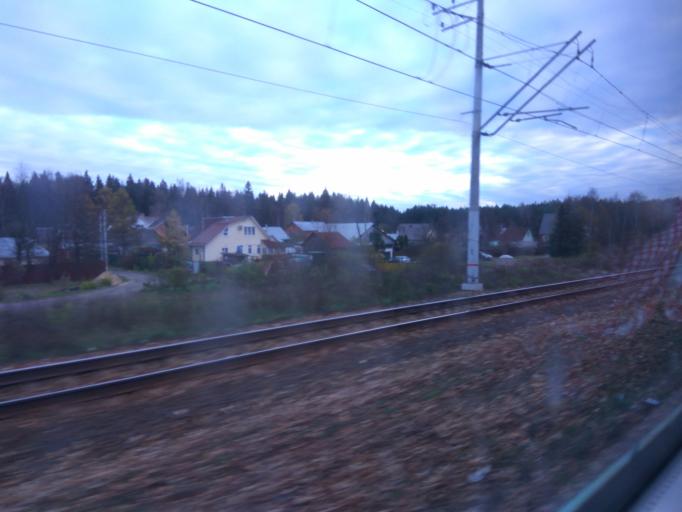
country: RU
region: Moskovskaya
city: Kievskij
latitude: 55.4782
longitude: 36.9139
